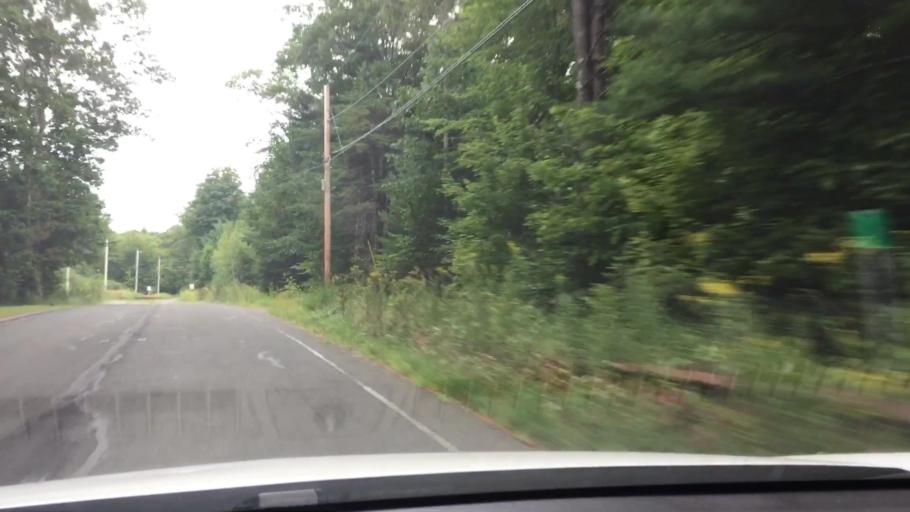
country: US
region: Massachusetts
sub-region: Berkshire County
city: Becket
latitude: 42.2604
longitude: -73.0000
